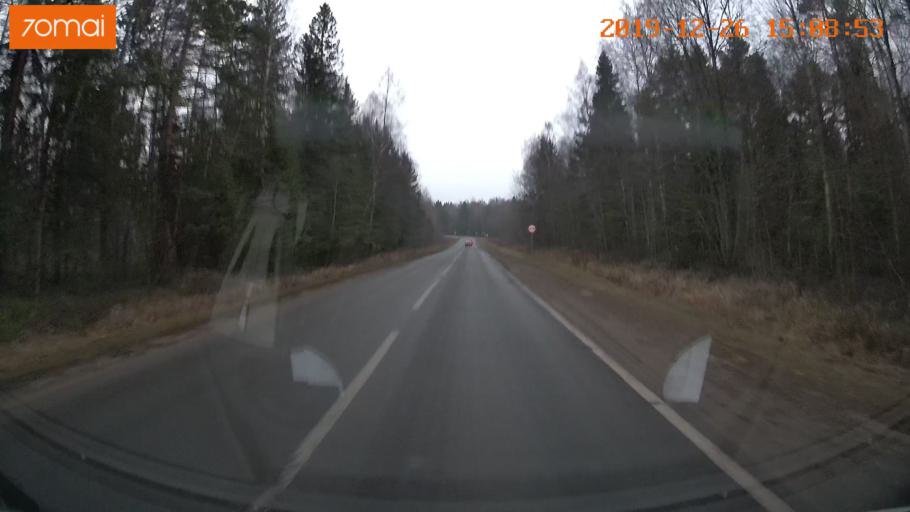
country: RU
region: Jaroslavl
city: Rybinsk
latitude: 58.1547
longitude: 38.8374
